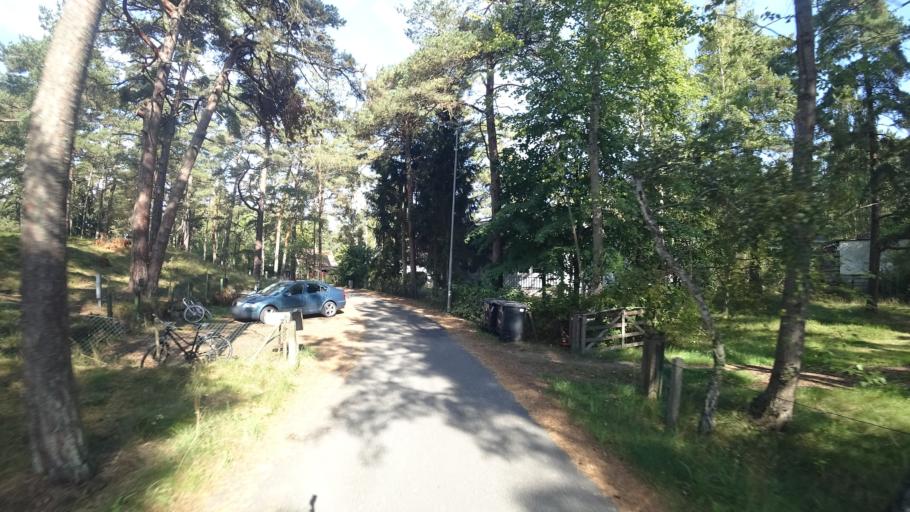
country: SE
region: Skane
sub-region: Kristianstads Kommun
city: Ahus
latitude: 55.9176
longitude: 14.3039
